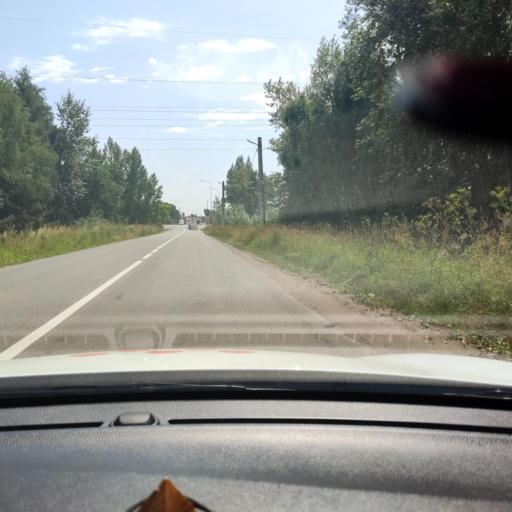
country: RU
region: Tatarstan
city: Osinovo
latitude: 55.9048
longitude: 48.9627
